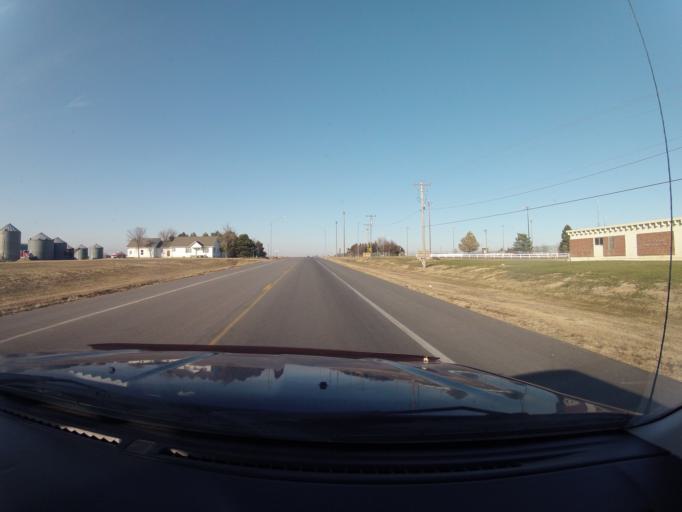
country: US
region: Nebraska
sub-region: Kearney County
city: Minden
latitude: 40.5149
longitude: -98.9519
